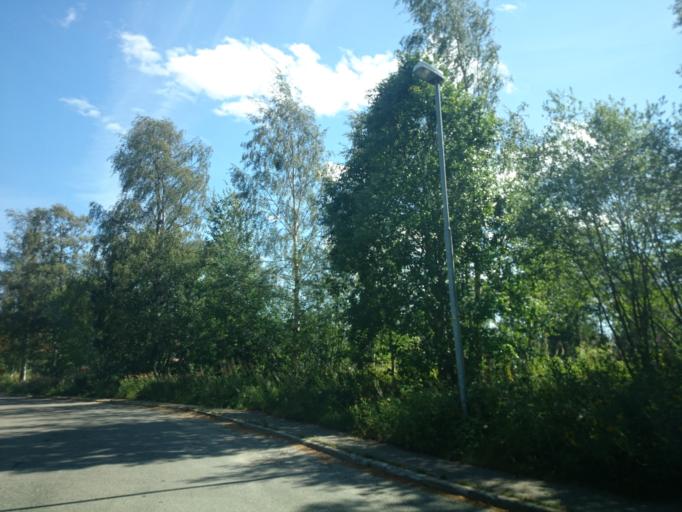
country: SE
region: Gaevleborg
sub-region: Ljusdals Kommun
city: Jaervsoe
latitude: 61.7077
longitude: 16.1616
